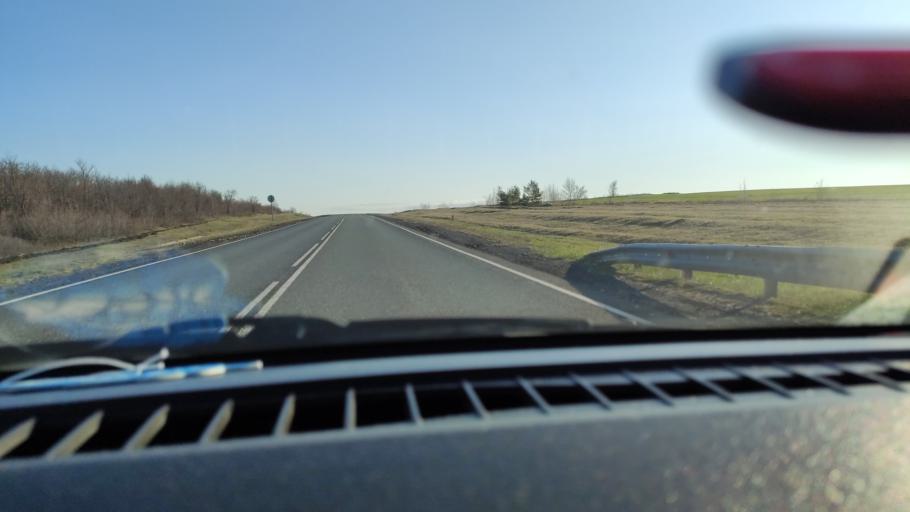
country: RU
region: Saratov
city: Balakovo
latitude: 52.1910
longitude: 47.8534
